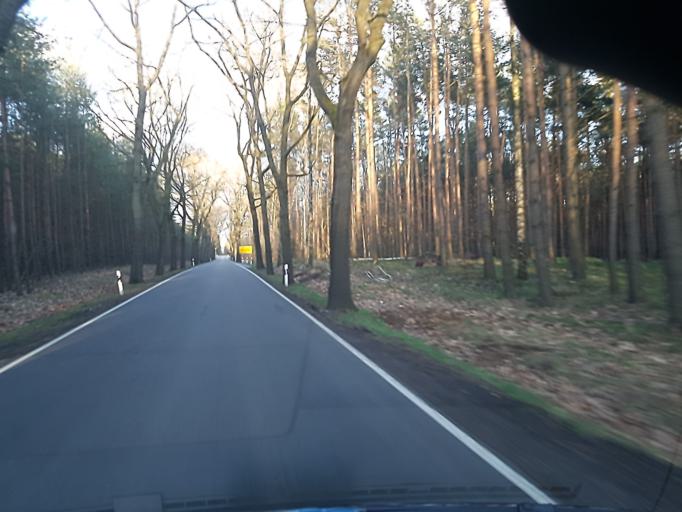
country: DE
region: Saxony
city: Trossin
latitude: 51.5657
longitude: 12.7837
